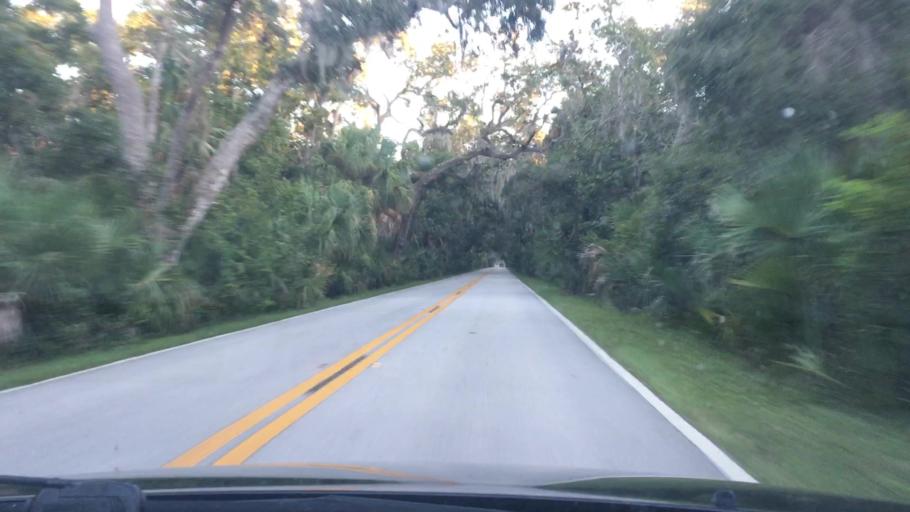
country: US
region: Florida
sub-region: Volusia County
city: Ormond-by-the-Sea
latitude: 29.3324
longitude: -81.0795
